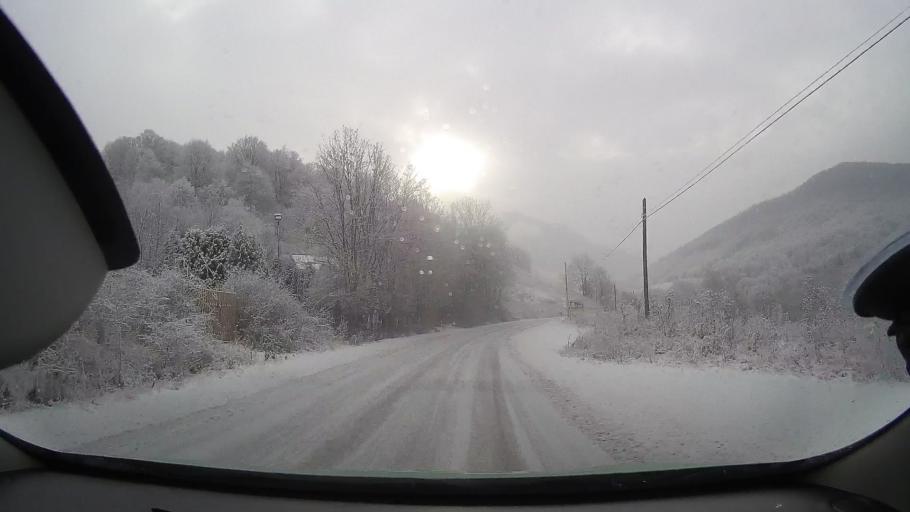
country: RO
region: Alba
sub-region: Comuna Rimetea
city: Rimetea
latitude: 46.4819
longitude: 23.5805
